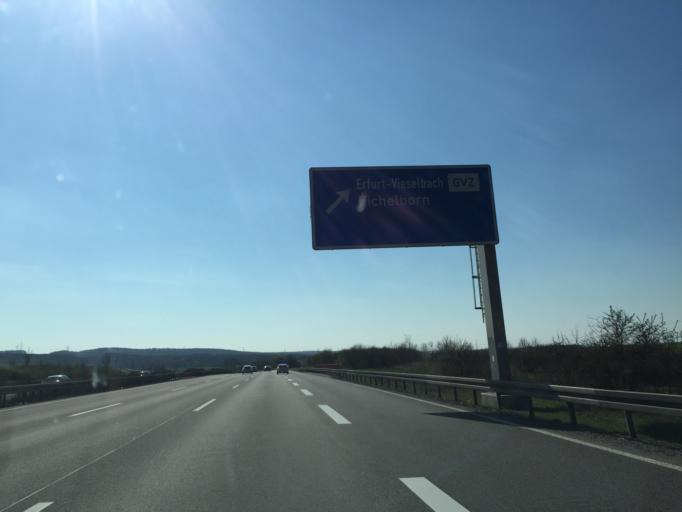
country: DE
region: Thuringia
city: Bechstedtstrass
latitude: 50.9450
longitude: 11.1749
